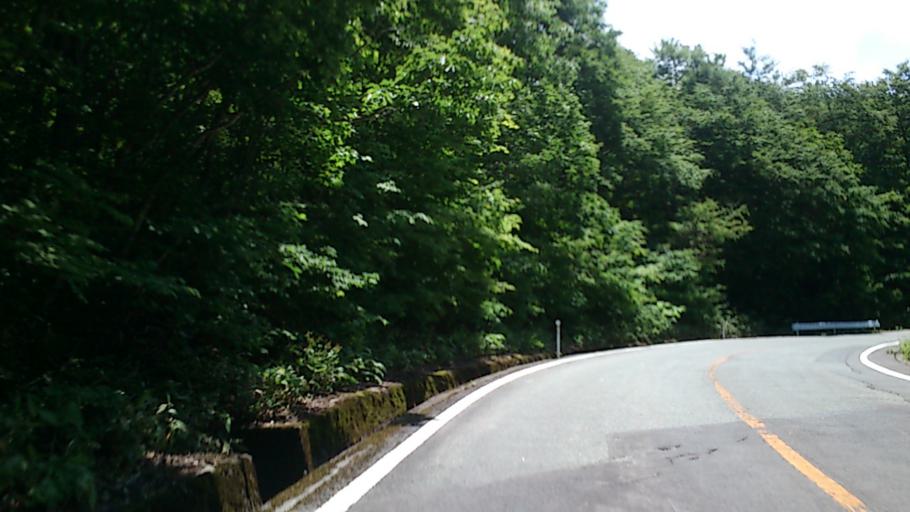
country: JP
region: Yamagata
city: Yamagata-shi
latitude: 38.1215
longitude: 140.4108
